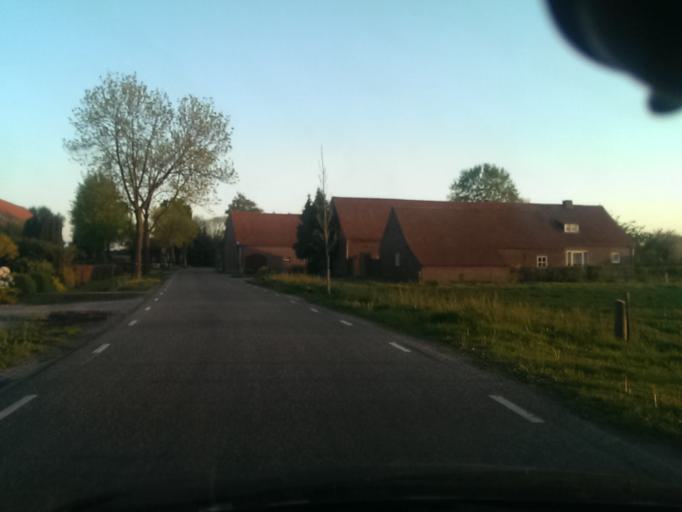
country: NL
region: Limburg
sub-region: Gemeente Nederweert
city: Nederweert
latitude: 51.2950
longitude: 5.7895
